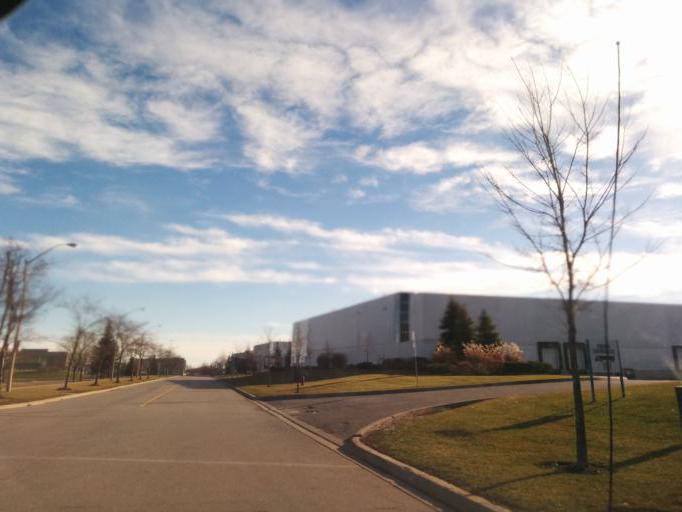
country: CA
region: Ontario
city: Oakville
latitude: 43.5062
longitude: -79.6801
